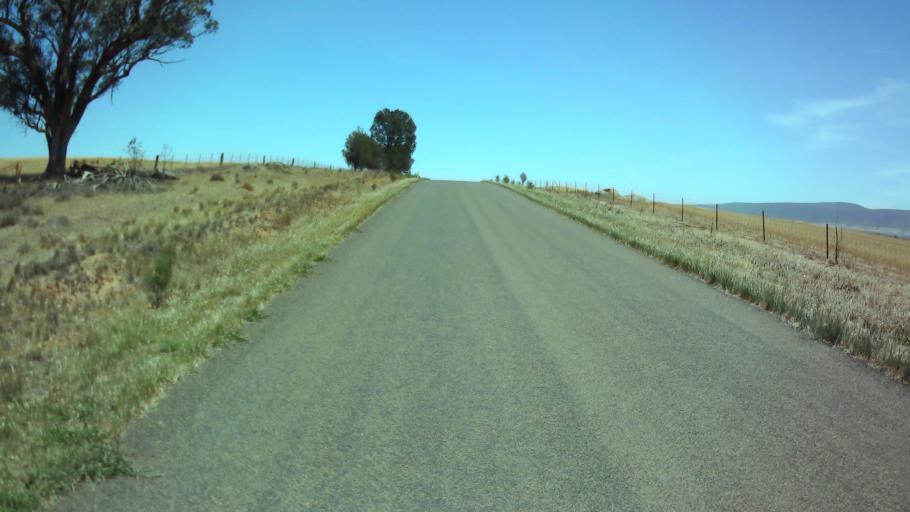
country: AU
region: New South Wales
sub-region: Weddin
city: Grenfell
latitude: -34.0500
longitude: 148.1821
